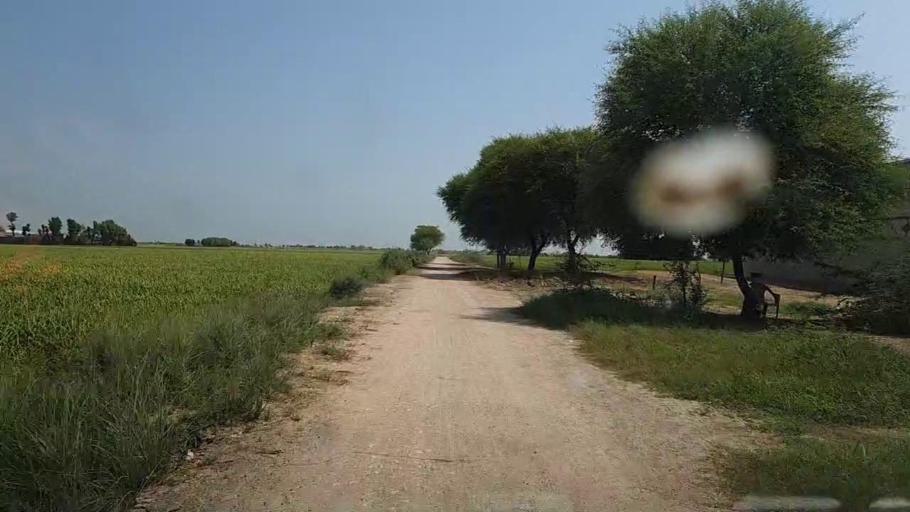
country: PK
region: Sindh
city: Kario
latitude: 24.6331
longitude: 68.5424
